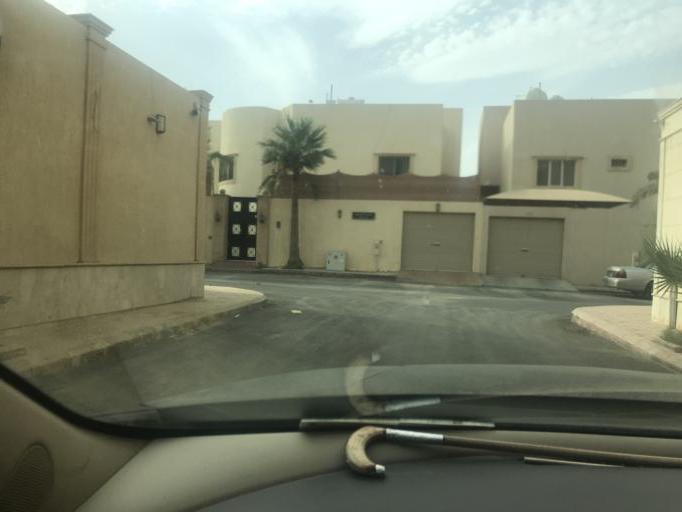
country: SA
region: Ar Riyad
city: Riyadh
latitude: 24.7978
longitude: 46.6694
